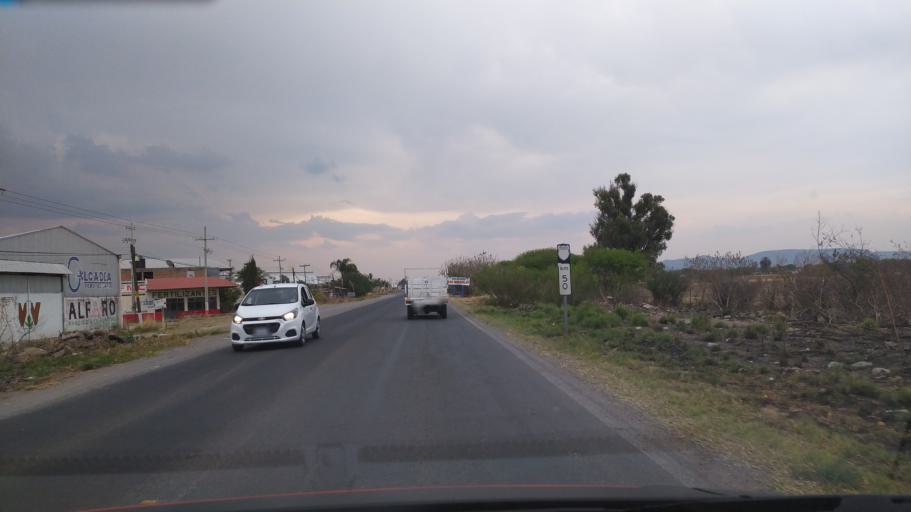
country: MX
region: Guanajuato
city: Ciudad Manuel Doblado
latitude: 20.7368
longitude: -101.9343
